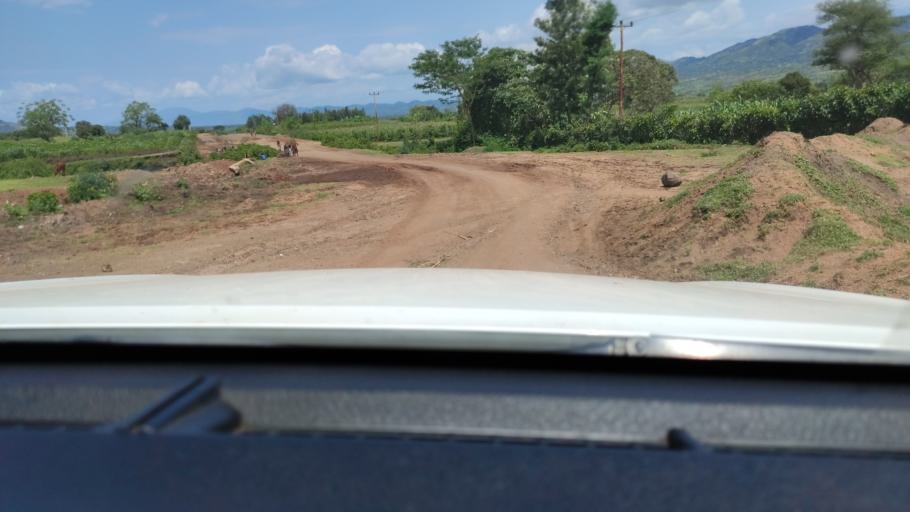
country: ET
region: Southern Nations, Nationalities, and People's Region
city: Felege Neway
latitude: 6.3656
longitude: 36.9909
